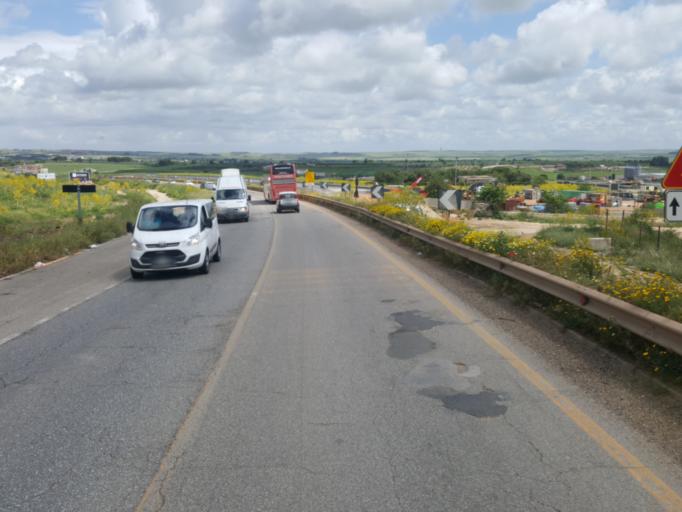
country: IT
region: Apulia
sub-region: Provincia di Bari
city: Altamura
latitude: 40.8173
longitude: 16.5678
